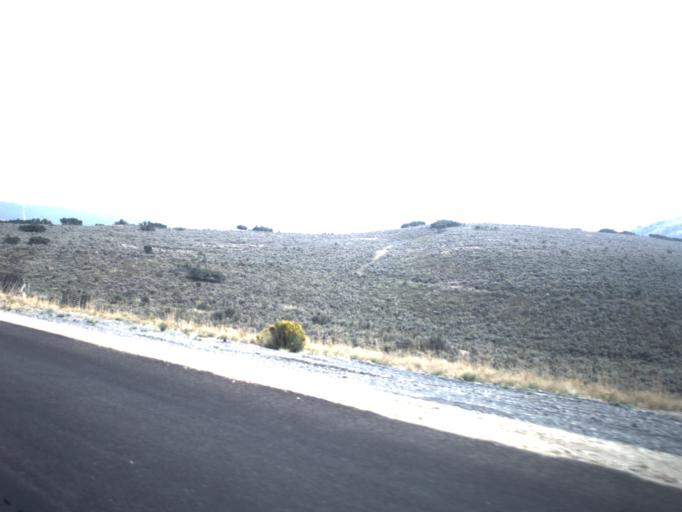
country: US
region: Utah
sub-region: Summit County
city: Park City
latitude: 40.6807
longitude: -111.4414
